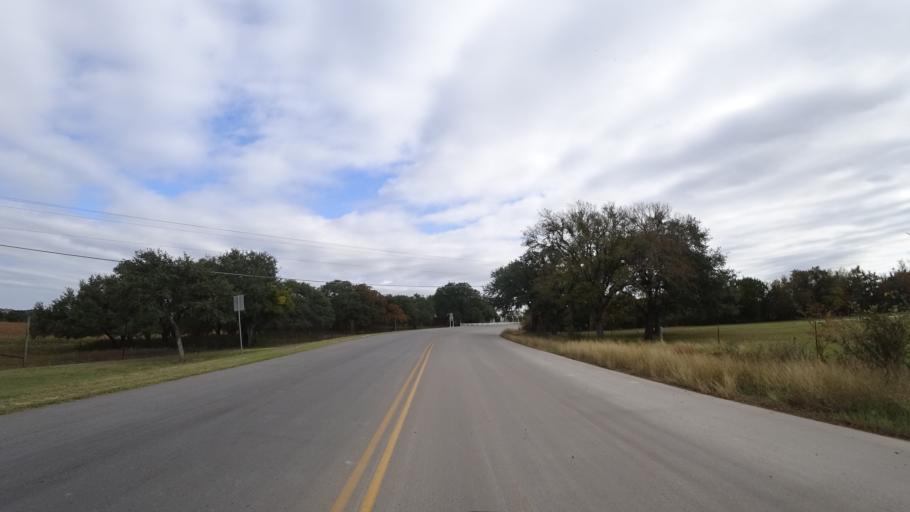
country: US
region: Texas
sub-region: Travis County
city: Manchaca
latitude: 30.1374
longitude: -97.8589
